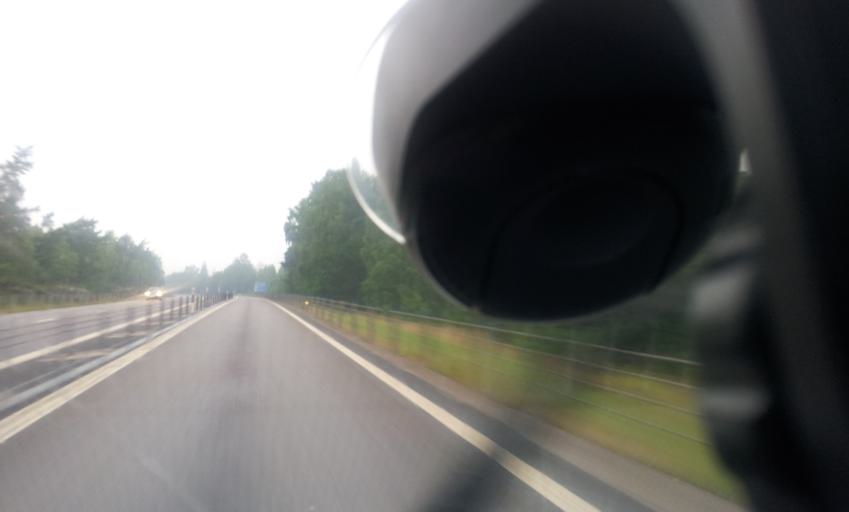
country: SE
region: Kalmar
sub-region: Vasterviks Kommun
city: Gamleby
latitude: 57.8160
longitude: 16.4816
